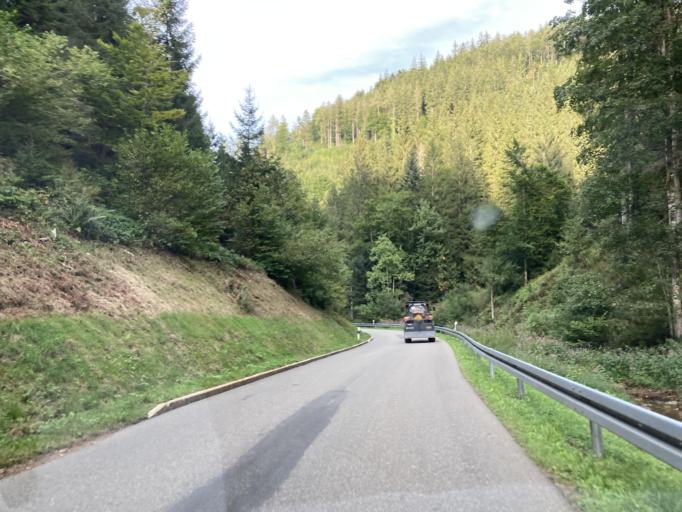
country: DE
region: Baden-Wuerttemberg
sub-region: Freiburg Region
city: Sankt Margen
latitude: 47.9943
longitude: 8.1268
